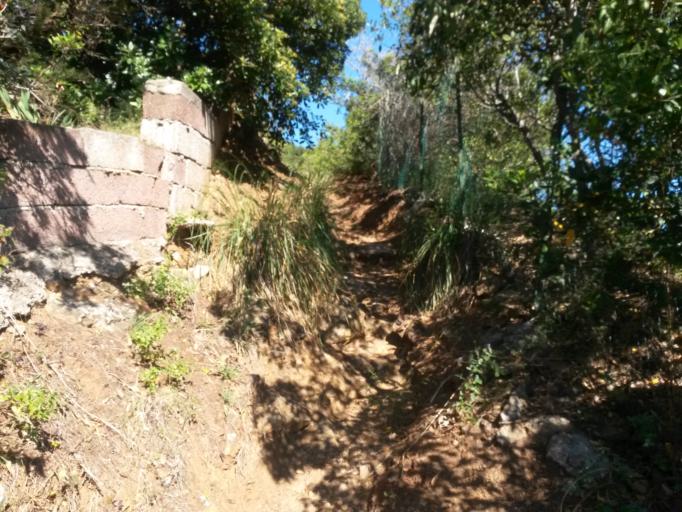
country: IT
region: Tuscany
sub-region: Provincia di Livorno
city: Porto Azzurro
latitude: 42.7697
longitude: 10.4149
